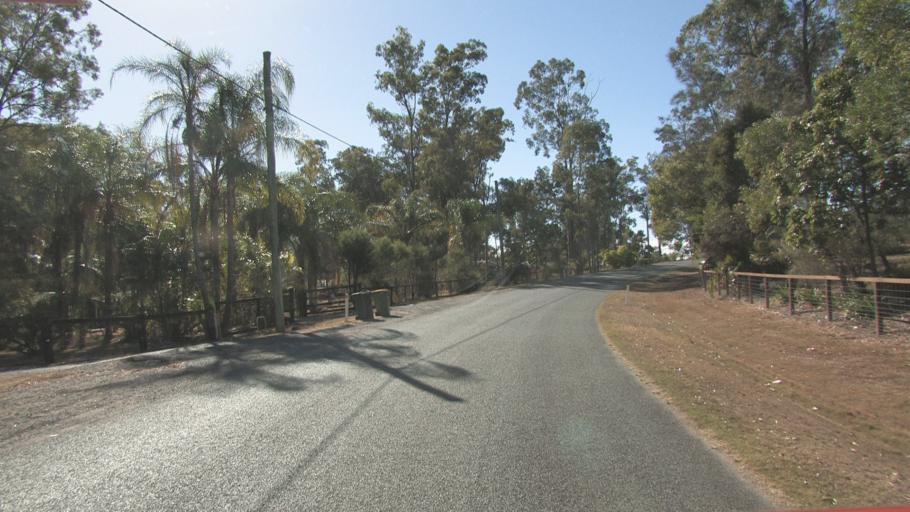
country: AU
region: Queensland
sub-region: Logan
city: Cedar Vale
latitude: -27.8827
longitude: 153.0012
